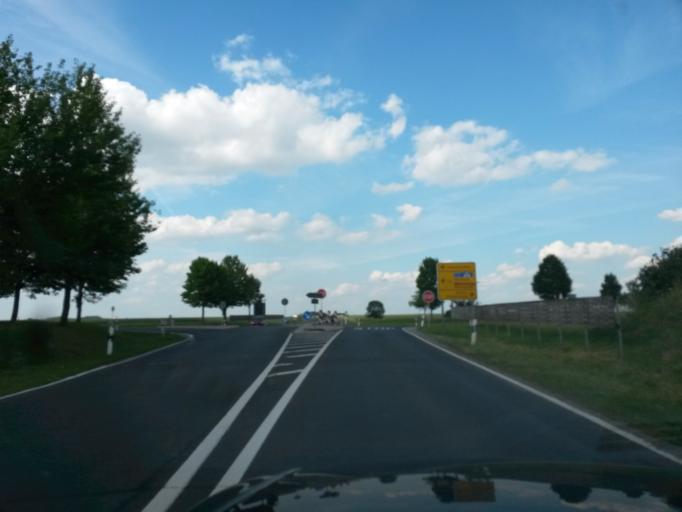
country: DE
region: Bavaria
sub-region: Regierungsbezirk Unterfranken
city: Kurnach
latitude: 49.8510
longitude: 10.0304
